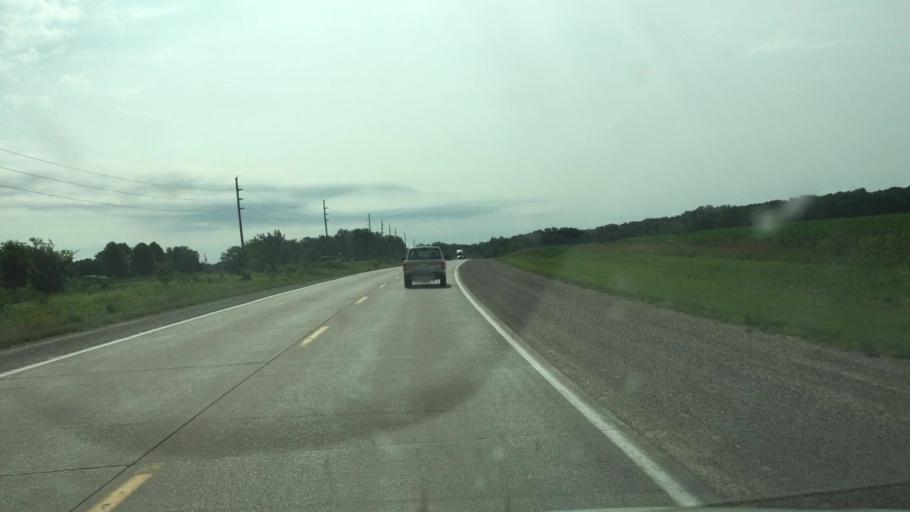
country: US
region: Illinois
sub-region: Hancock County
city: Nauvoo
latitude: 40.6317
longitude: -91.4989
